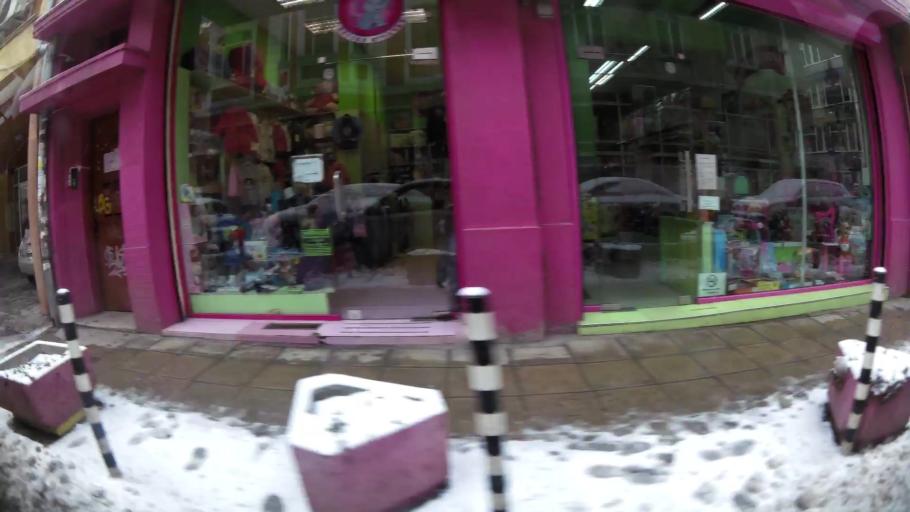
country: BG
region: Sofia-Capital
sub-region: Stolichna Obshtina
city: Sofia
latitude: 42.6965
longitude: 23.3195
